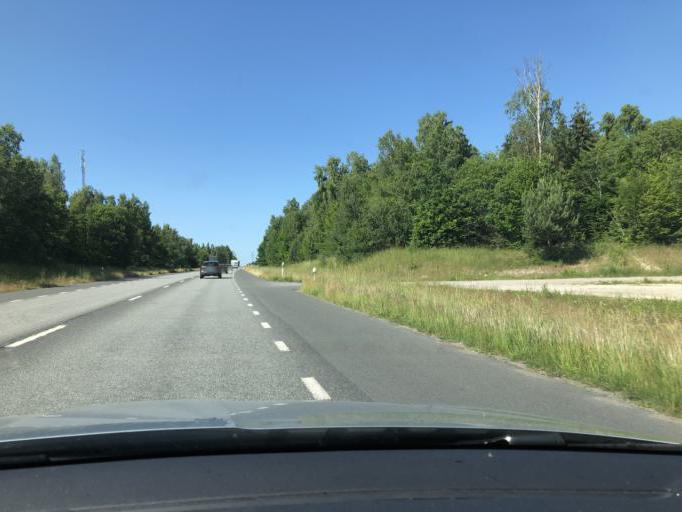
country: SE
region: Skane
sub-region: Bromolla Kommun
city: Bromoella
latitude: 56.0696
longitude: 14.4988
